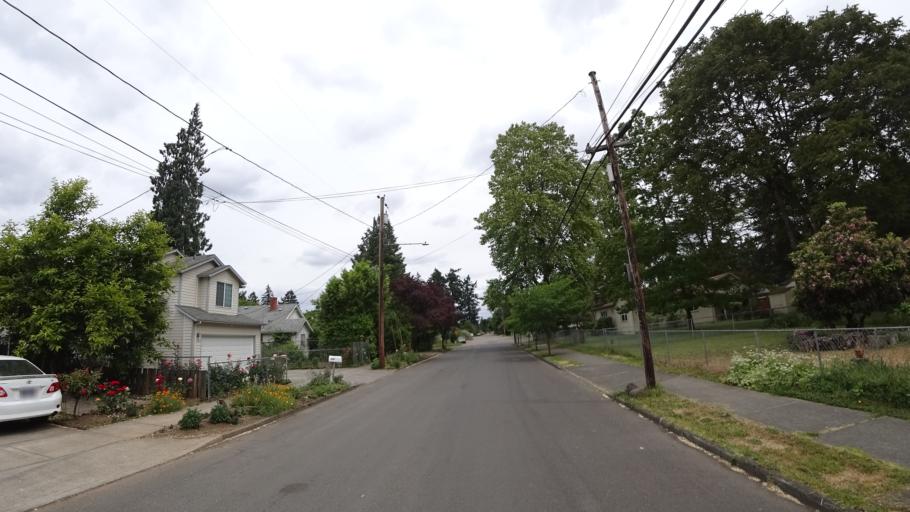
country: US
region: Oregon
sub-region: Multnomah County
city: Lents
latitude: 45.5026
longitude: -122.5522
